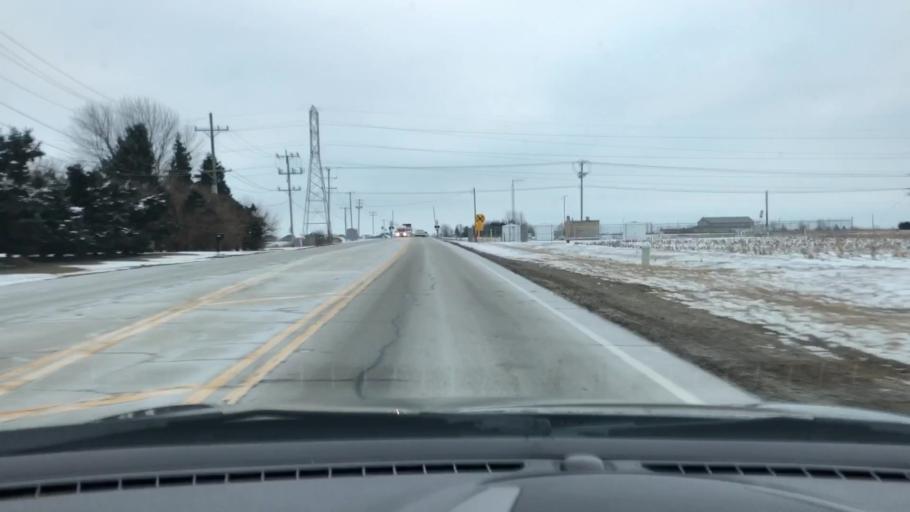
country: US
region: Illinois
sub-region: Will County
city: New Lenox
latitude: 41.4936
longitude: -88.0038
